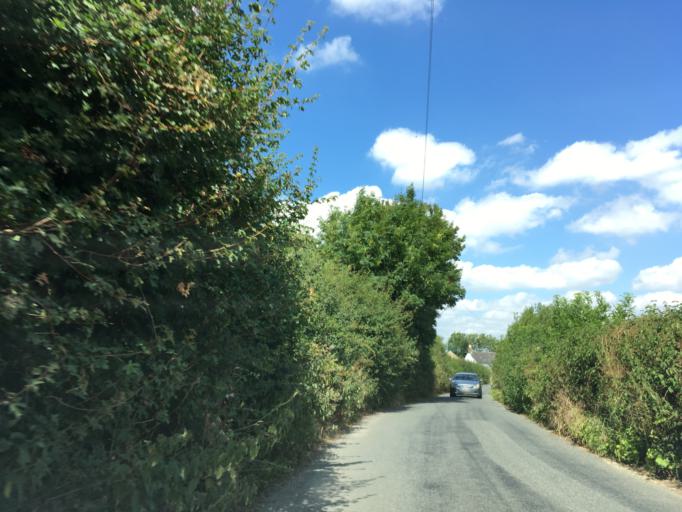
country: GB
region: England
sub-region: Gloucestershire
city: Shurdington
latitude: 51.8533
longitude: -2.1308
